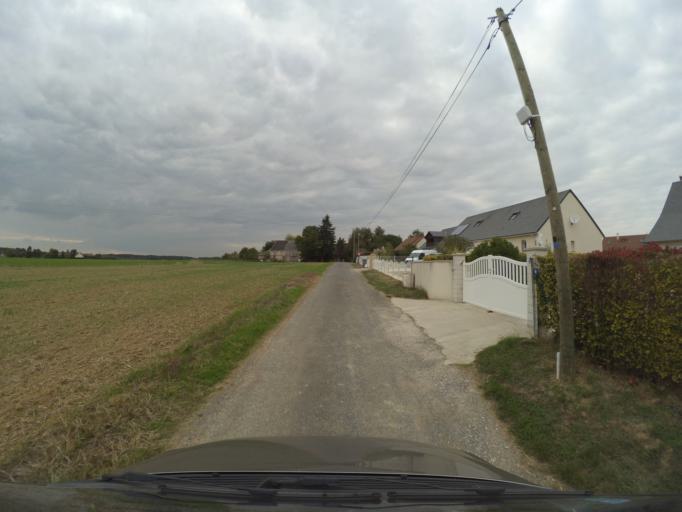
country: FR
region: Centre
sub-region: Departement d'Indre-et-Loire
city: Reugny
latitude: 47.4799
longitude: 0.9121
